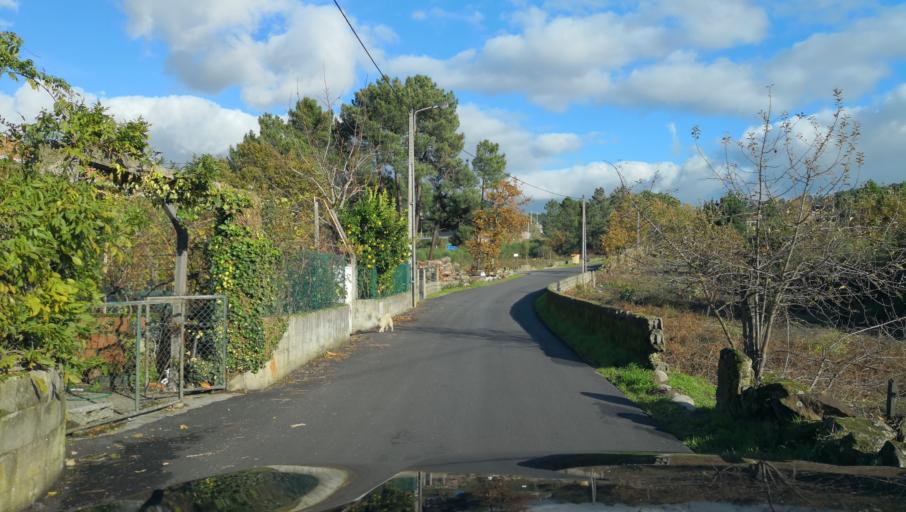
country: PT
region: Vila Real
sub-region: Vila Real
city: Vila Real
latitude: 41.3152
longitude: -7.7212
